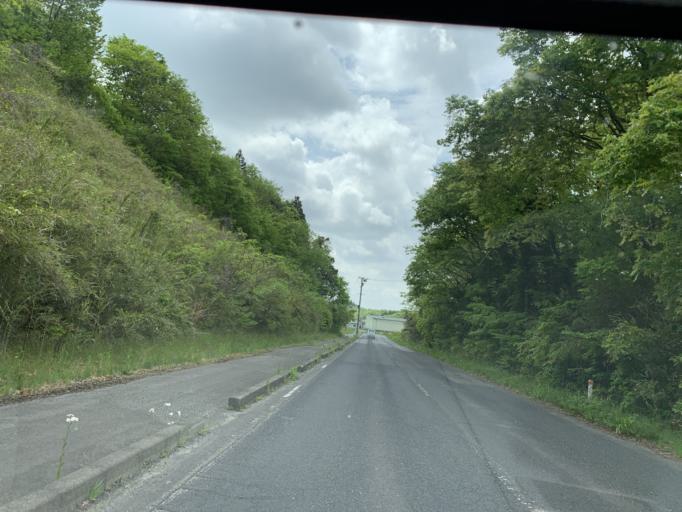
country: JP
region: Miyagi
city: Furukawa
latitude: 38.6986
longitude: 140.9272
